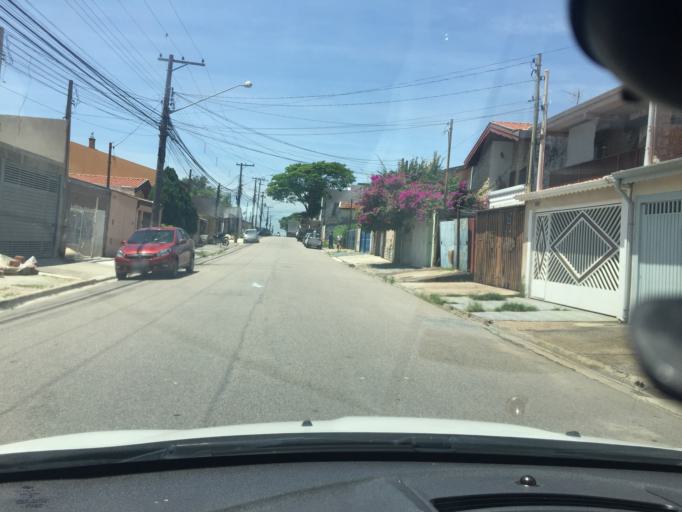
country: BR
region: Sao Paulo
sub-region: Jundiai
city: Jundiai
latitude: -23.2275
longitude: -46.8812
